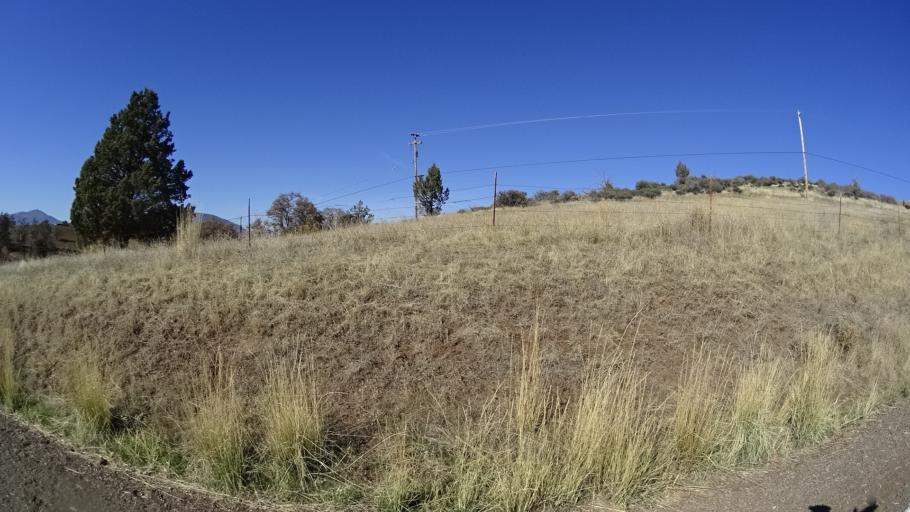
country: US
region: California
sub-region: Siskiyou County
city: Montague
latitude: 41.8079
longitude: -122.3826
